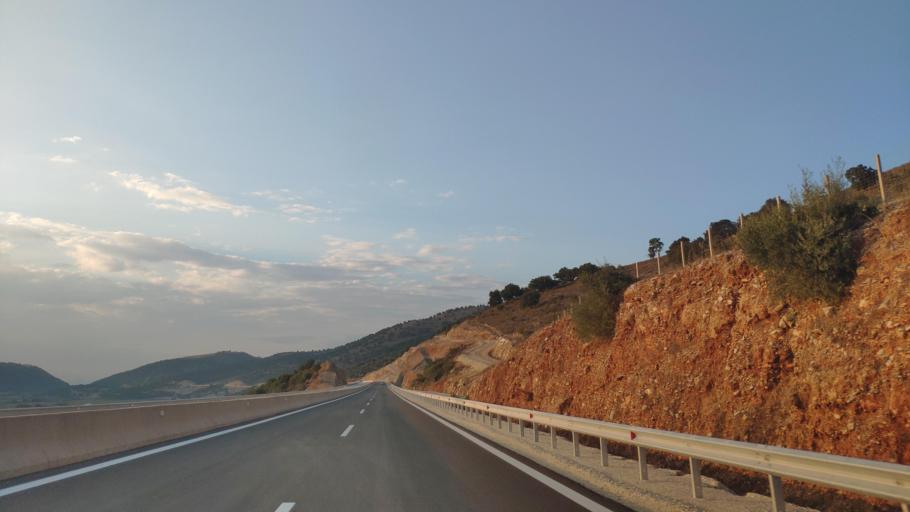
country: GR
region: West Greece
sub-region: Nomos Aitolias kai Akarnanias
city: Katouna
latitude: 38.8137
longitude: 21.1285
